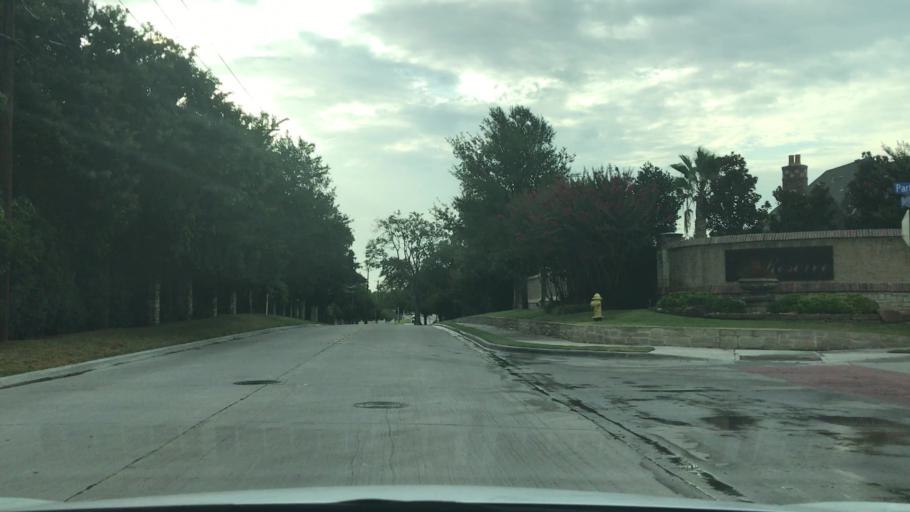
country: US
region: Texas
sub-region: Dallas County
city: Coppell
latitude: 32.9546
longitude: -97.0009
